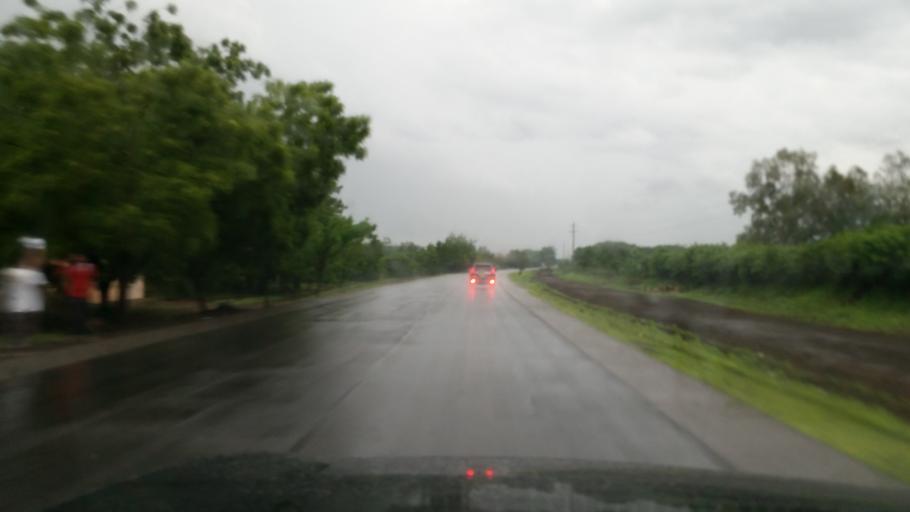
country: NI
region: Chinandega
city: Puerto Morazan
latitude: 12.7960
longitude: -86.9821
